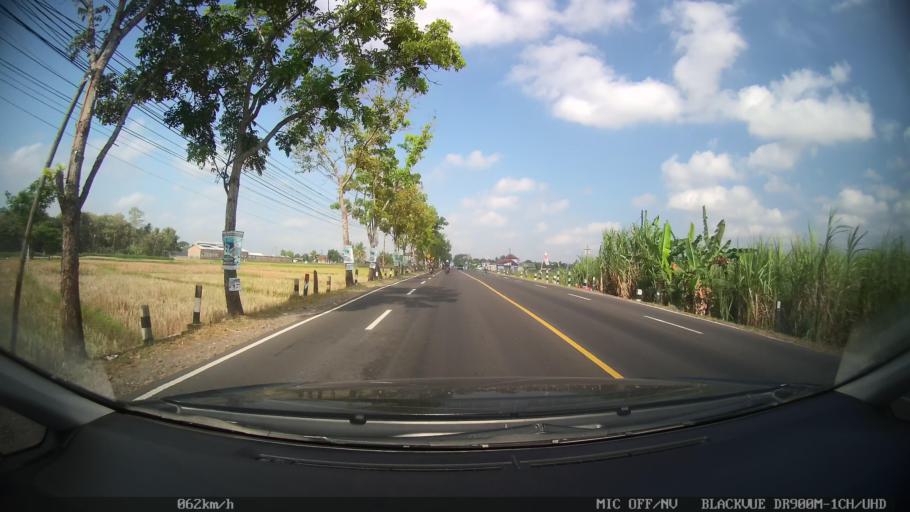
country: ID
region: Daerah Istimewa Yogyakarta
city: Godean
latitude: -7.8181
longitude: 110.2457
